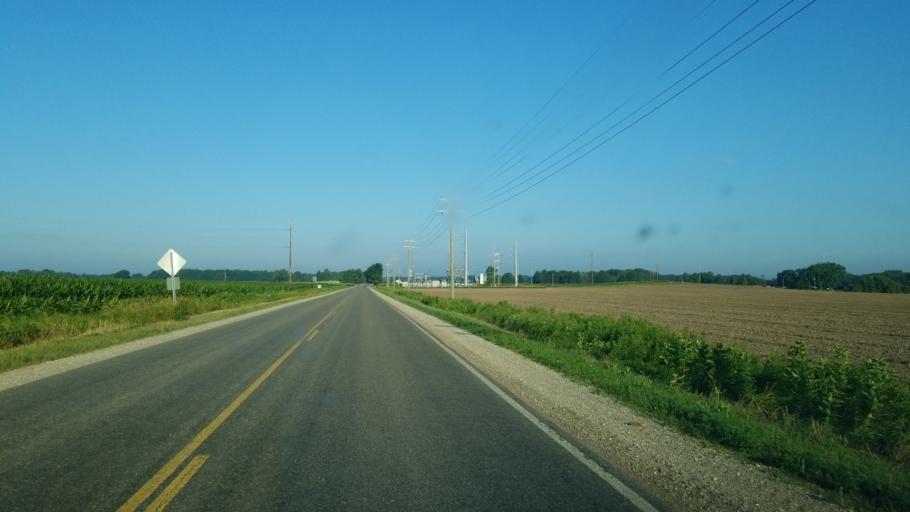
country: US
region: Michigan
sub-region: Mecosta County
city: Canadian Lakes
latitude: 43.5398
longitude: -85.2295
